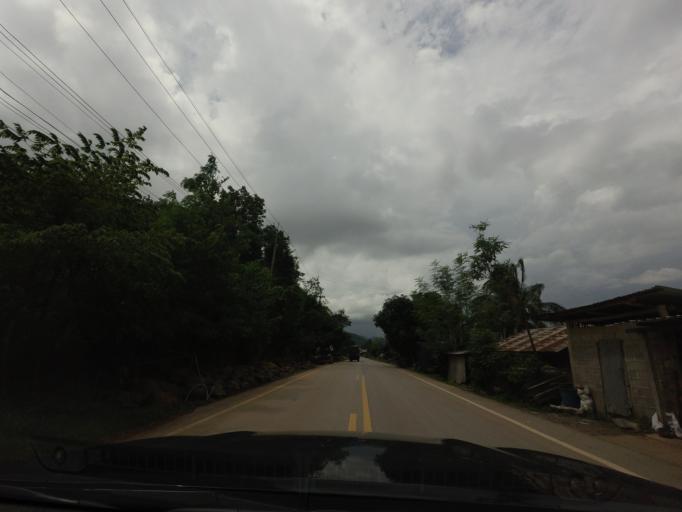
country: TH
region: Loei
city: Pak Chom
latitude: 18.0554
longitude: 101.8070
